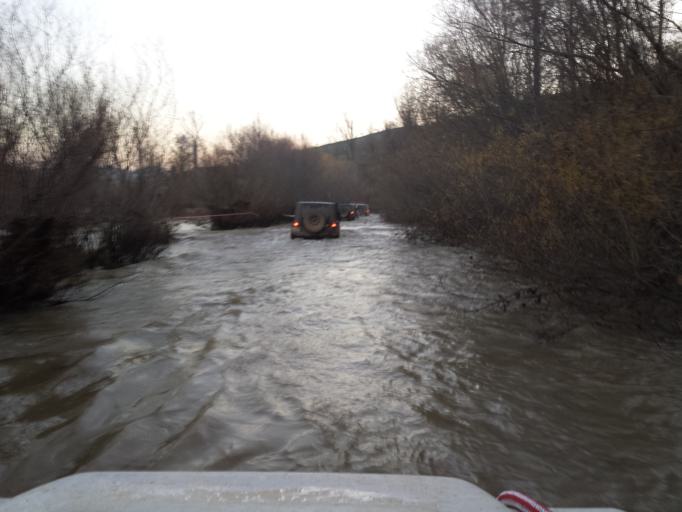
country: IT
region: Friuli Venezia Giulia
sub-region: Provincia di Udine
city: Corno di Rosazzo
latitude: 46.0011
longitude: 13.4606
